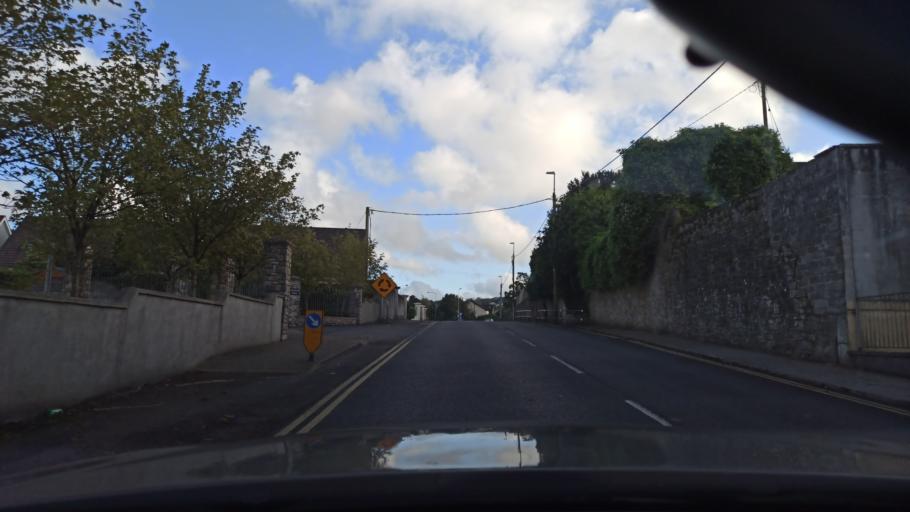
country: IE
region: Munster
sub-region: North Tipperary
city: Roscrea
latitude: 52.9501
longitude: -7.7975
